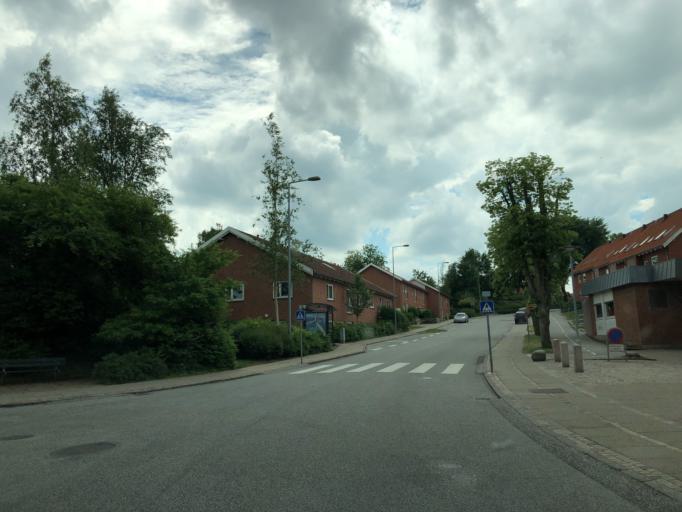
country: DK
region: Central Jutland
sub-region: Struer Kommune
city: Struer
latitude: 56.4906
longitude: 8.5908
